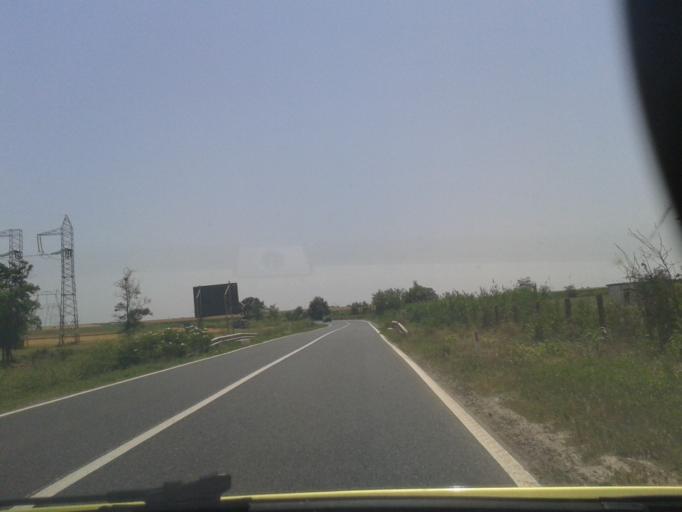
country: RO
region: Constanta
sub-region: Comuna Mihail Kogalniceanu
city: Mihail Kogalniceanu
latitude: 44.3580
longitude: 28.5189
